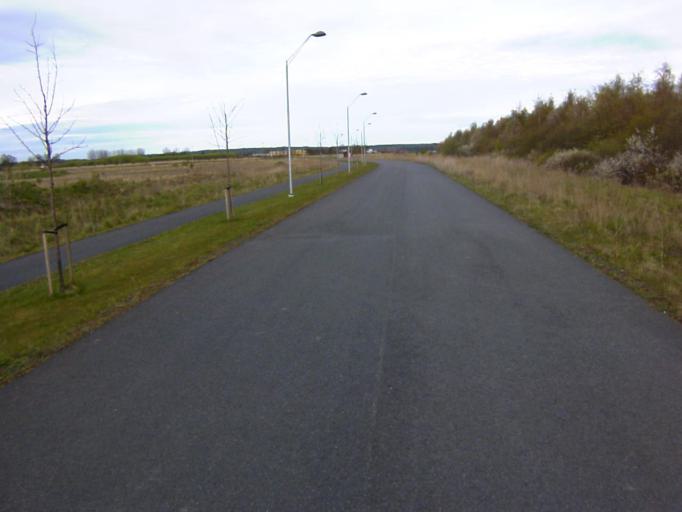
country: SE
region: Skane
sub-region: Kristianstads Kommun
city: Kristianstad
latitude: 56.0259
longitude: 14.1191
